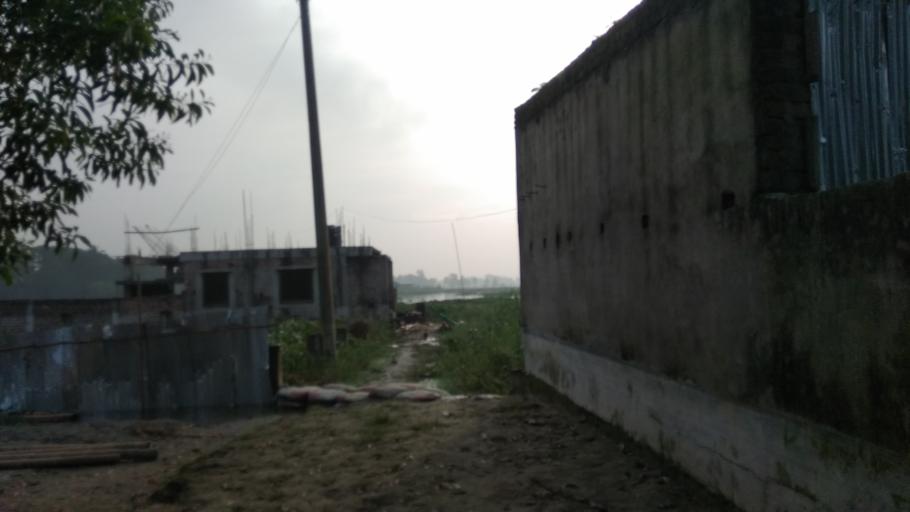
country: BD
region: Dhaka
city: Tungi
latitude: 23.8517
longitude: 90.4433
